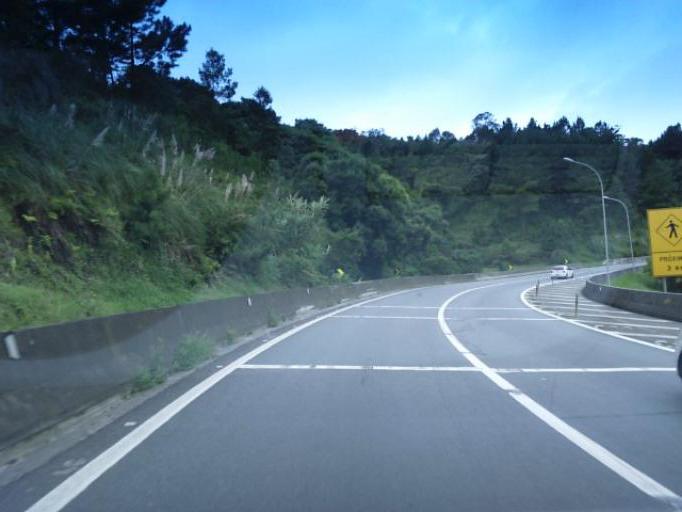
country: BR
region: Parana
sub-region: Campina Grande Do Sul
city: Campina Grande do Sul
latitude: -25.1094
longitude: -48.8433
